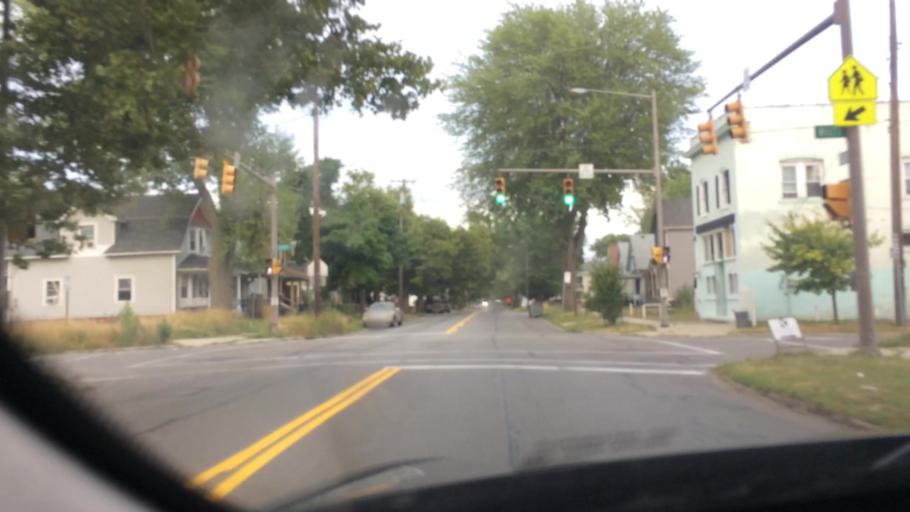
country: US
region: Ohio
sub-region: Wood County
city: Rossford
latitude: 41.6308
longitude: -83.5726
